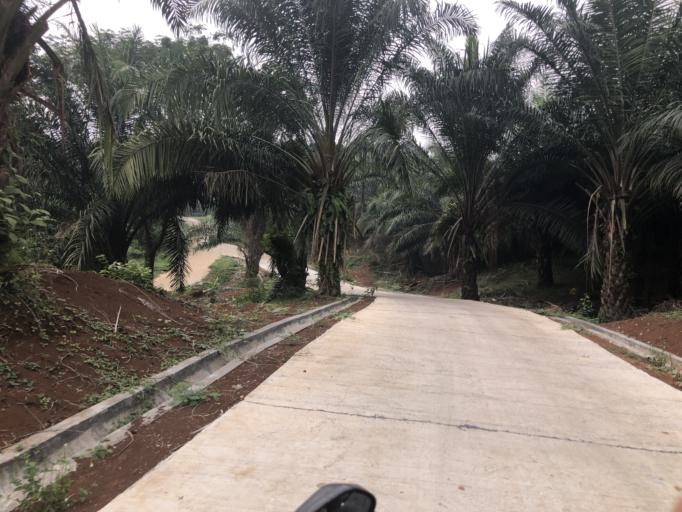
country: ID
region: West Java
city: Ciampea
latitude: -6.5488
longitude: 106.7155
